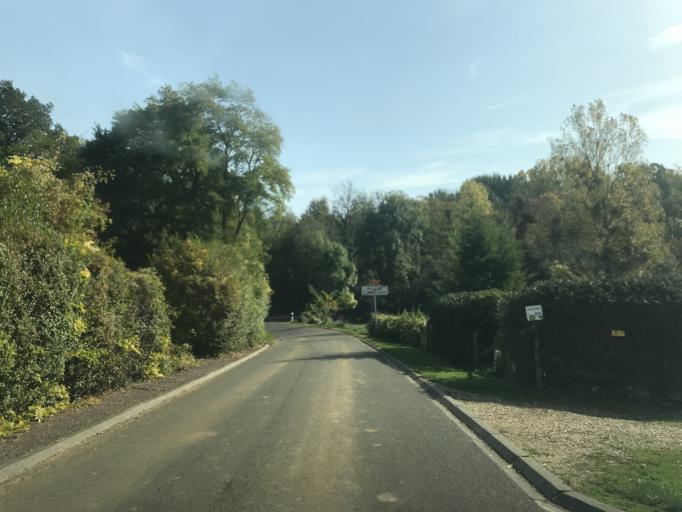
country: FR
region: Haute-Normandie
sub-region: Departement de l'Eure
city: La Chapelle-Reanville
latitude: 49.1108
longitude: 1.3829
